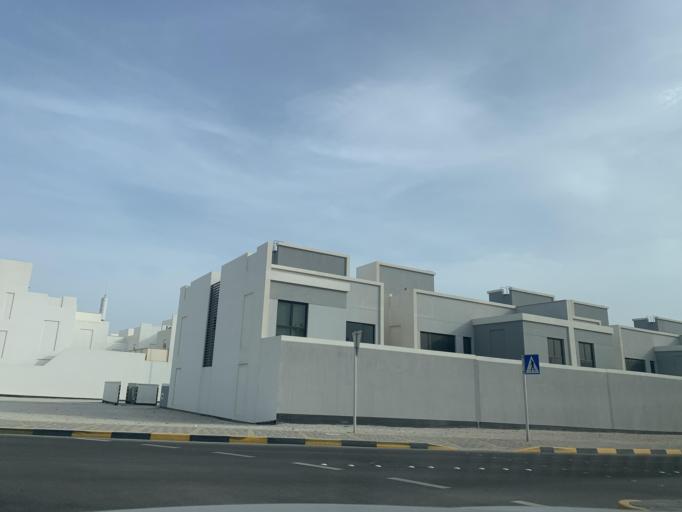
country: BH
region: Muharraq
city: Al Muharraq
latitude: 26.3148
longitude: 50.6291
